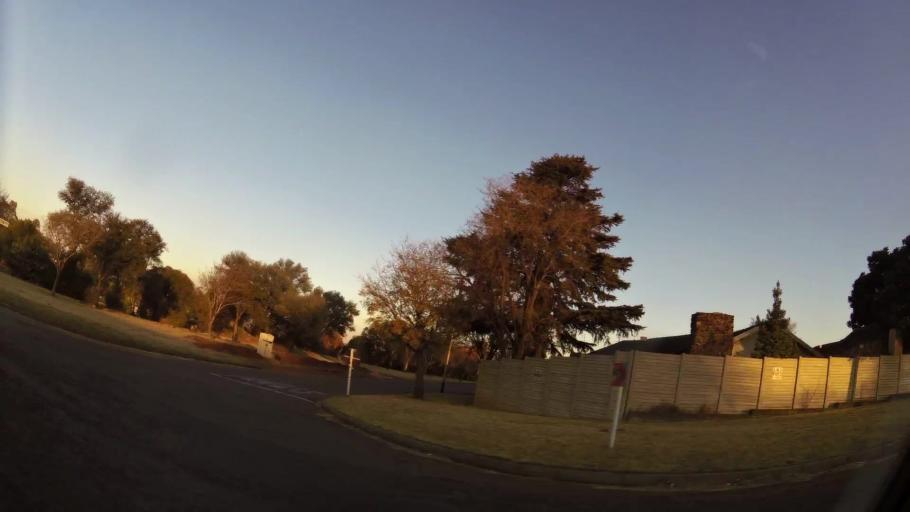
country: ZA
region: Gauteng
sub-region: Ekurhuleni Metropolitan Municipality
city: Germiston
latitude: -26.2596
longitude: 28.1630
